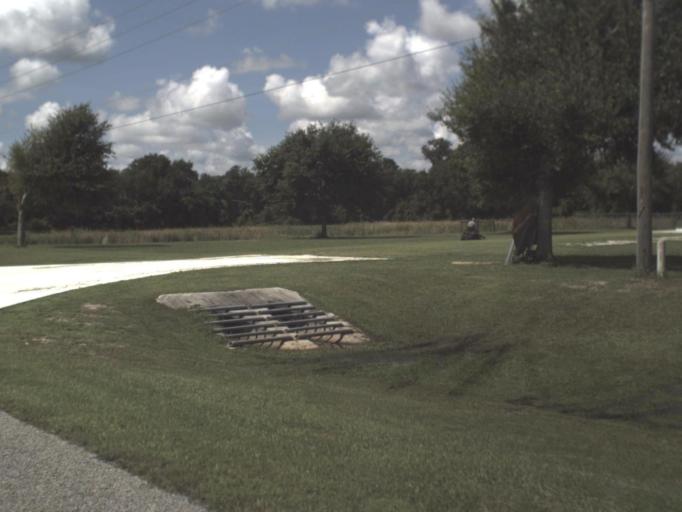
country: US
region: Florida
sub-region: DeSoto County
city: Arcadia
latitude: 27.2559
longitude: -81.8428
